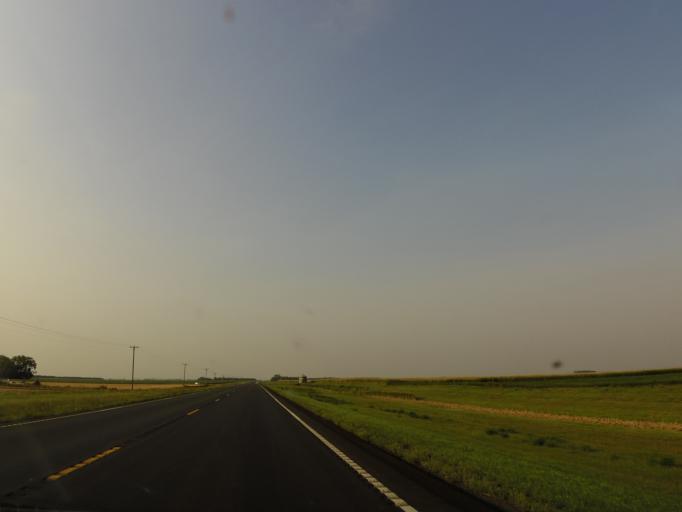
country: US
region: North Dakota
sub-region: Traill County
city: Mayville
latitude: 47.3731
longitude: -97.3264
